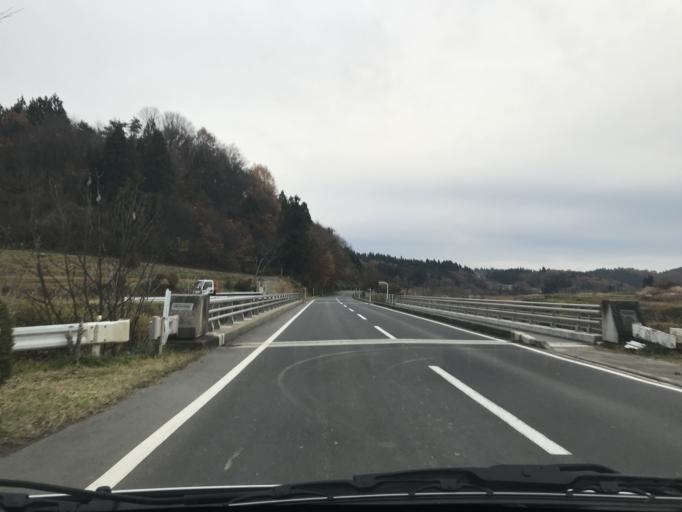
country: JP
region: Iwate
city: Kitakami
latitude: 39.2691
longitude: 141.2677
